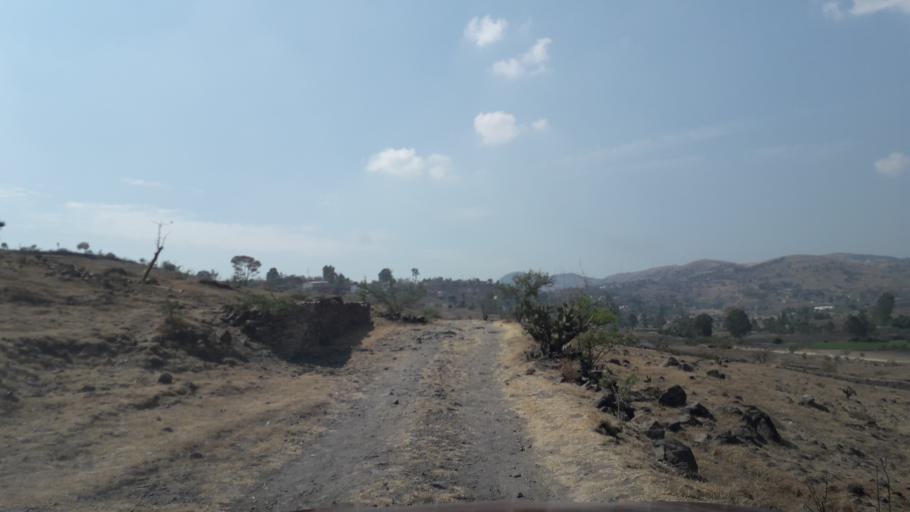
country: MX
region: Puebla
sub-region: Puebla
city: San Andres Azumiatla
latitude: 18.9147
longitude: -98.2595
